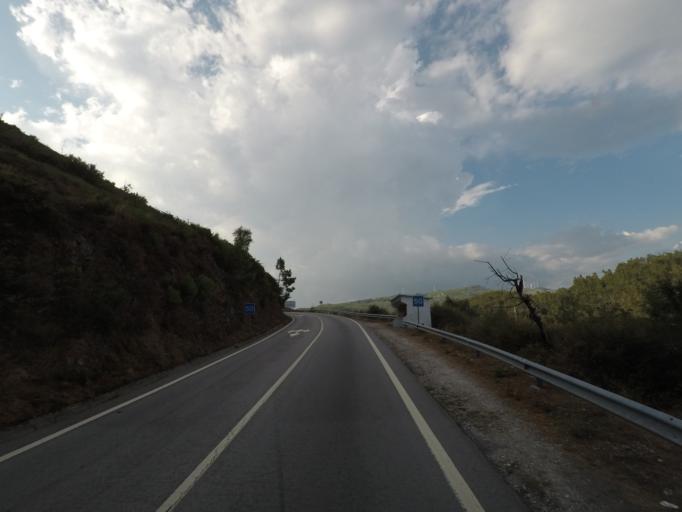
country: PT
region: Porto
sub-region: Baiao
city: Valadares
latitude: 41.1832
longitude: -7.9376
